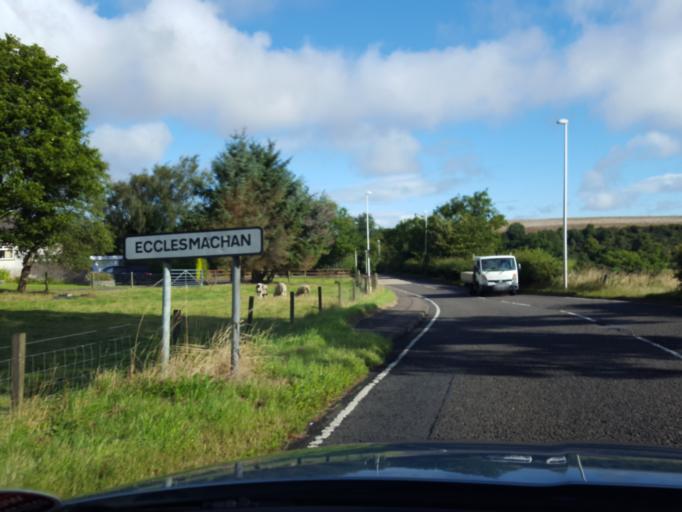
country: GB
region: Scotland
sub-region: West Lothian
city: Broxburn
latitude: 55.9435
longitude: -3.5076
